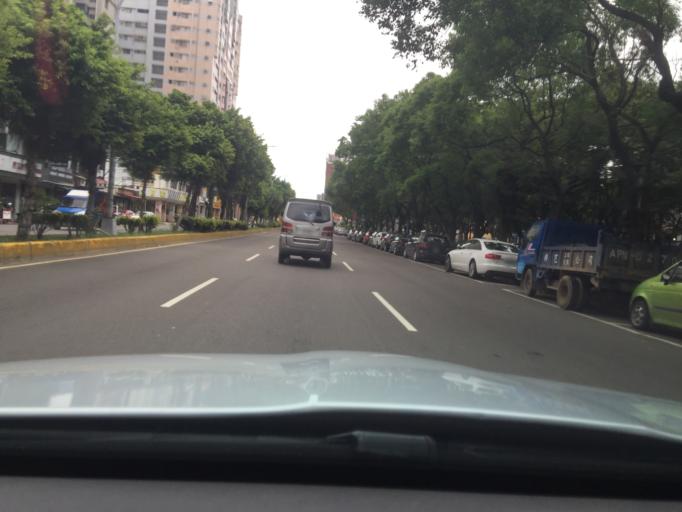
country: TW
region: Taiwan
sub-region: Hsinchu
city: Hsinchu
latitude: 24.8143
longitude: 120.9748
